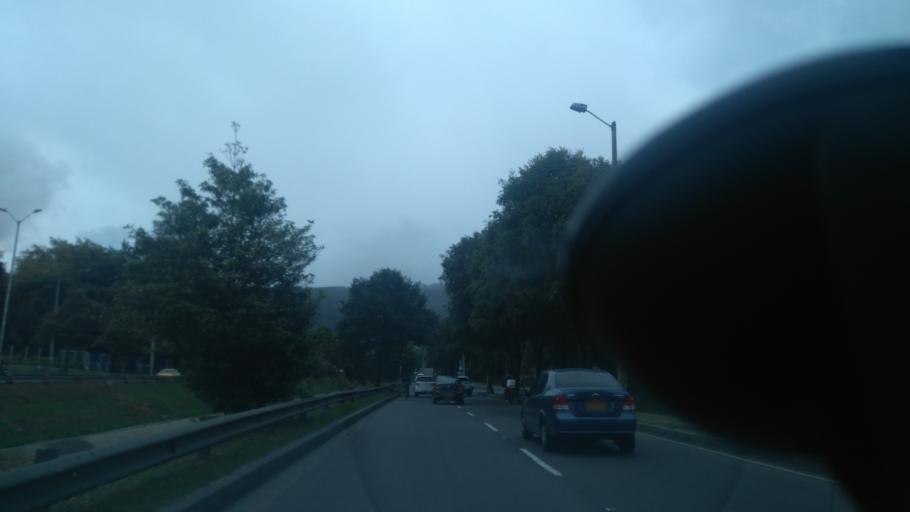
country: CO
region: Cundinamarca
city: La Calera
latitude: 4.7488
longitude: -74.0360
